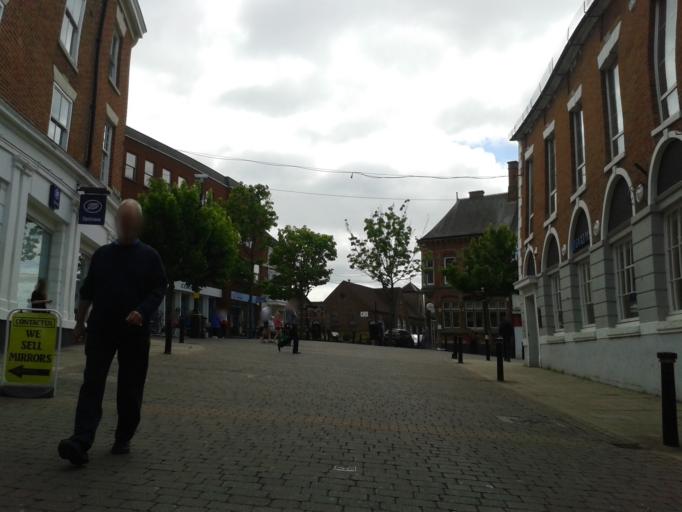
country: GB
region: England
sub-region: Leicestershire
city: Hinckley
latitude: 52.5414
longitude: -1.3731
